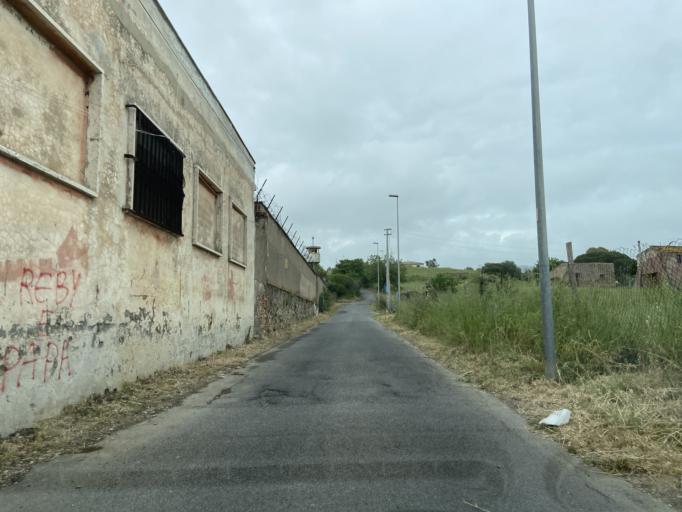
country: IT
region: Latium
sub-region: Citta metropolitana di Roma Capitale
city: Civitavecchia
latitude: 42.0888
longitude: 11.8118
